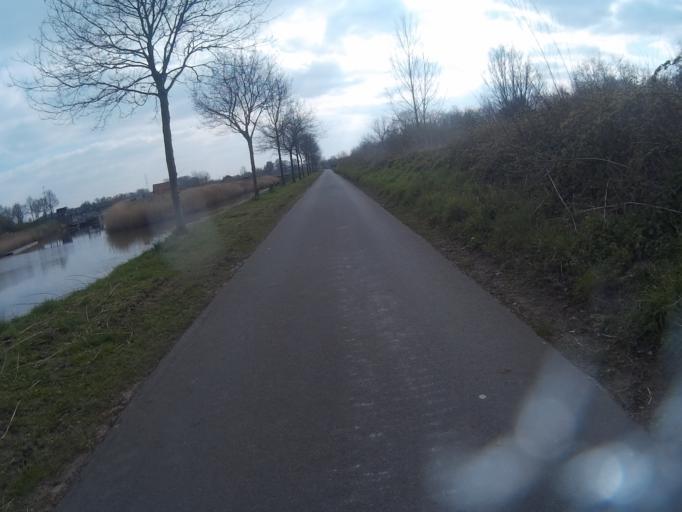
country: BE
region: Flanders
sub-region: Provincie Oost-Vlaanderen
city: Zomergem
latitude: 51.0975
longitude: 3.5634
